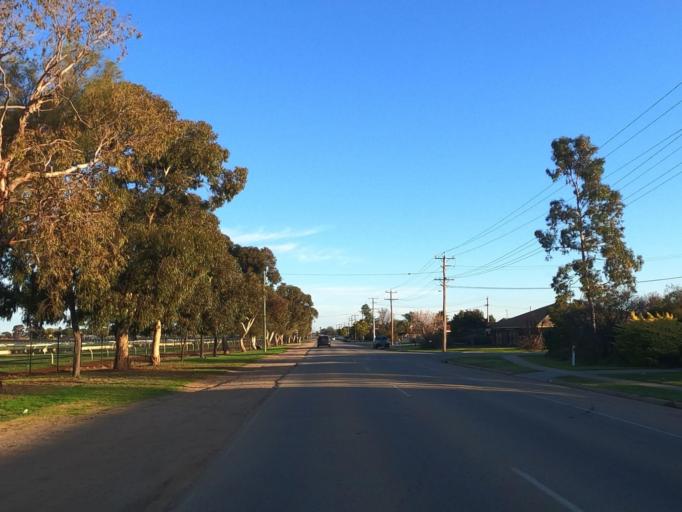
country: AU
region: Victoria
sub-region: Swan Hill
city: Swan Hill
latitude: -35.3496
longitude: 143.5546
